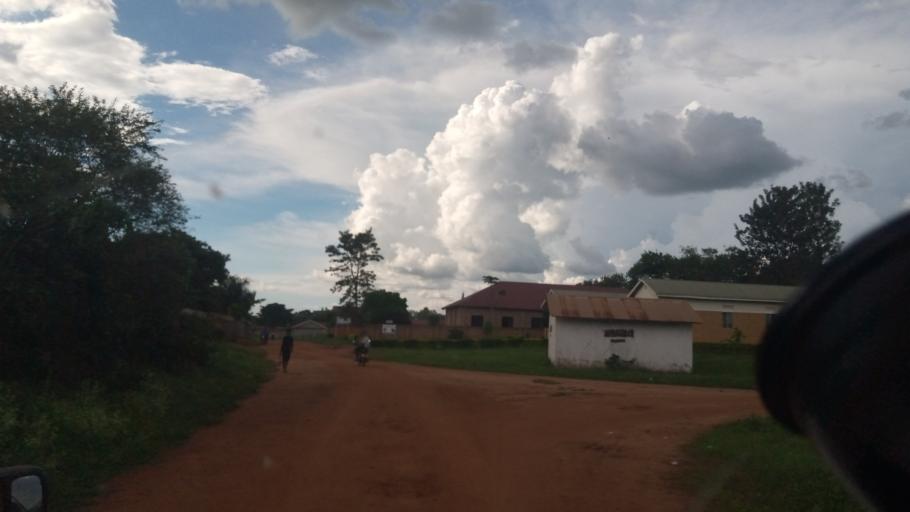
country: UG
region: Northern Region
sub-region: Lira District
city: Lira
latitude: 2.2402
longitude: 32.9008
